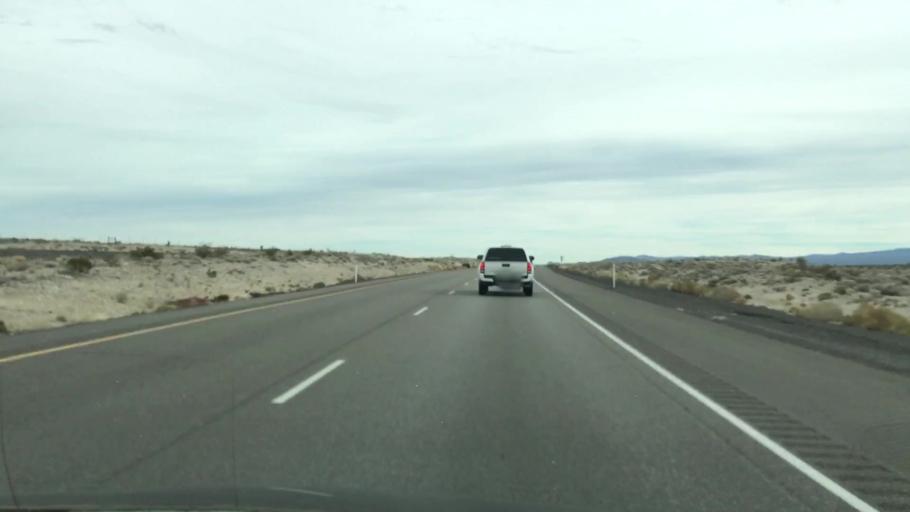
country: US
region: Nevada
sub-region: Nye County
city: Pahrump
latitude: 36.6002
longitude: -115.9640
